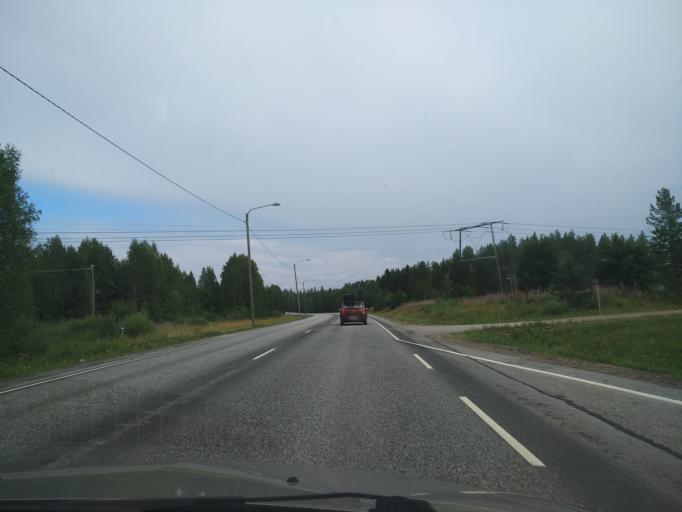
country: FI
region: Kainuu
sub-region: Kajaani
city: Paltamo
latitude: 64.4016
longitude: 27.8713
